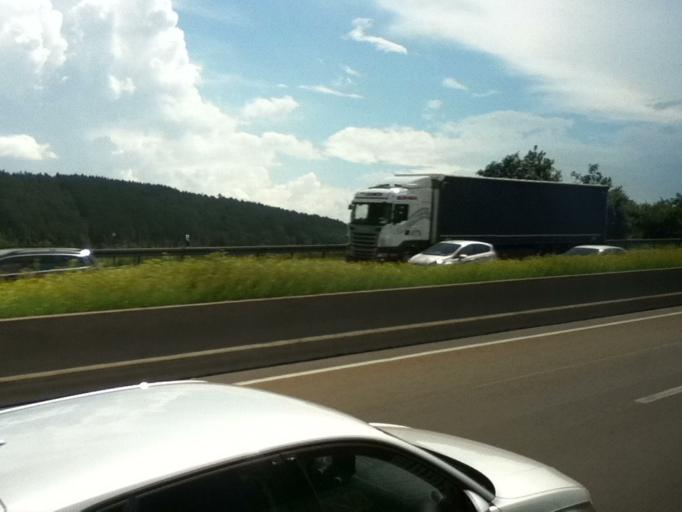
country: DE
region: Hesse
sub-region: Regierungsbezirk Kassel
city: Kirchheim
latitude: 50.8207
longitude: 9.5682
